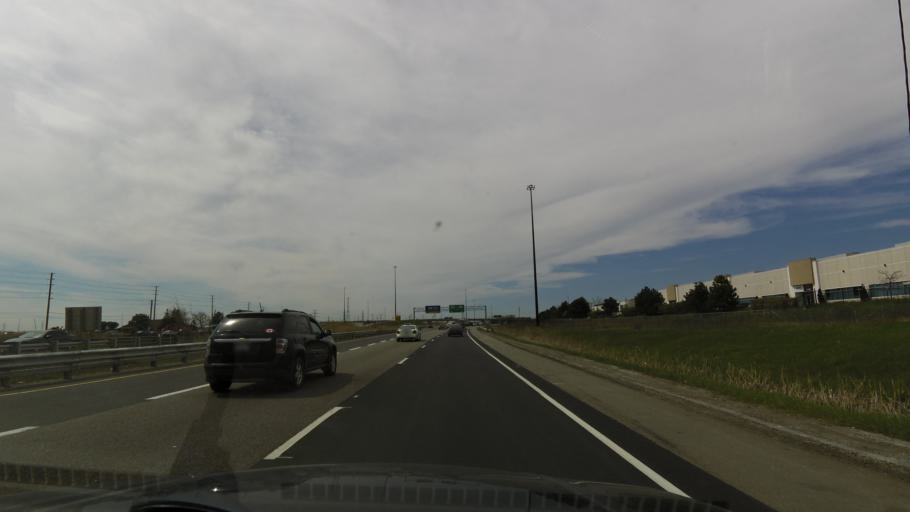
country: CA
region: Ontario
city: Mississauga
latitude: 43.5235
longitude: -79.7163
